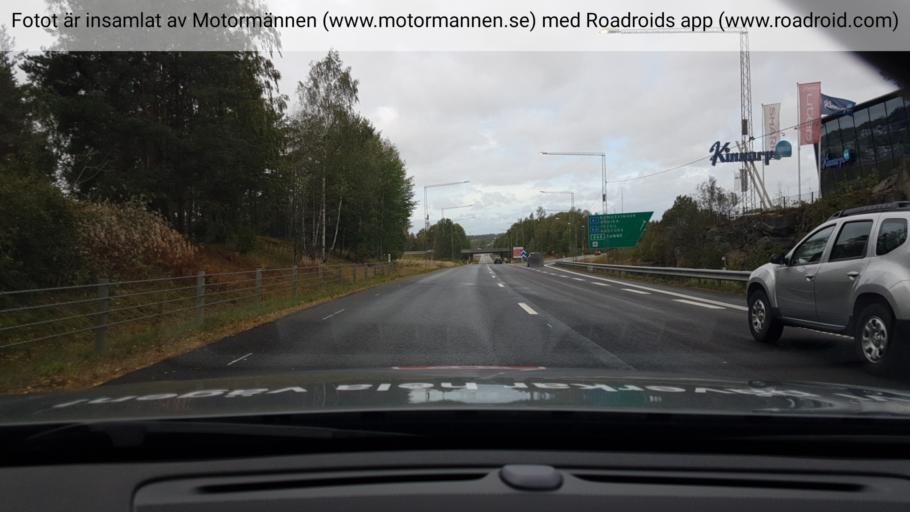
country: SE
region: Vaermland
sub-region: Hammaro Kommun
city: Skoghall
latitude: 59.3787
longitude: 13.4344
